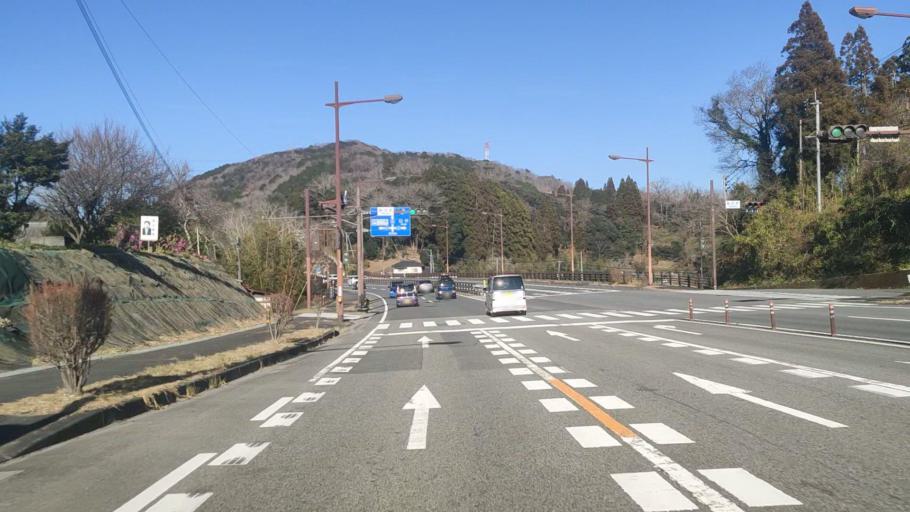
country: JP
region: Oita
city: Oita
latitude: 33.1085
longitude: 131.6561
